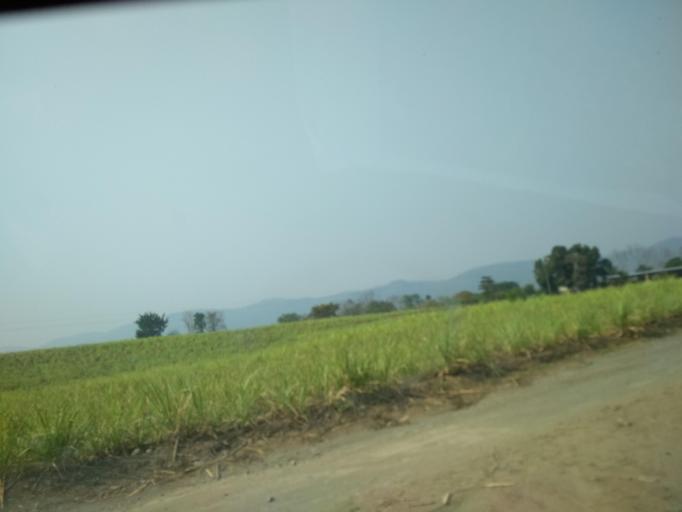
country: MX
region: Oaxaca
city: Acatlan de Perez Figueroa
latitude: 18.6082
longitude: -96.5725
